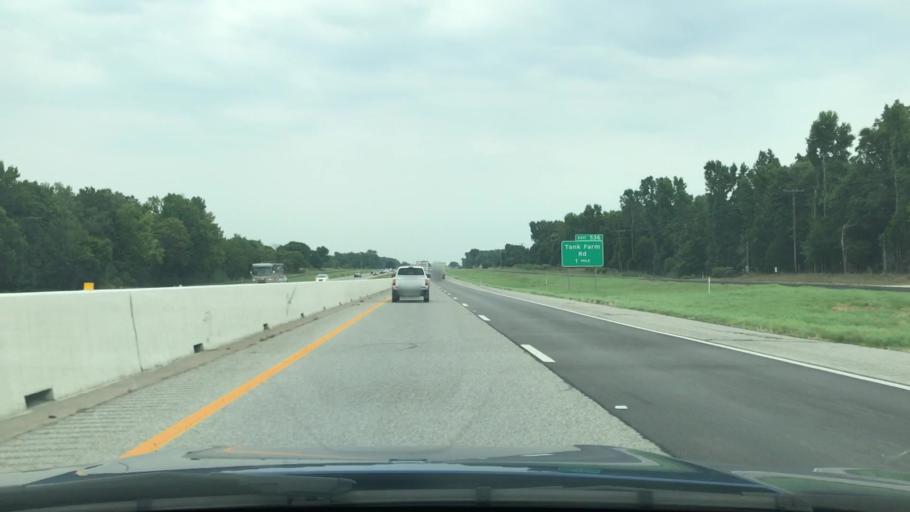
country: US
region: Texas
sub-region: Van Zandt County
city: Van
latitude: 32.5349
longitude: -95.7363
